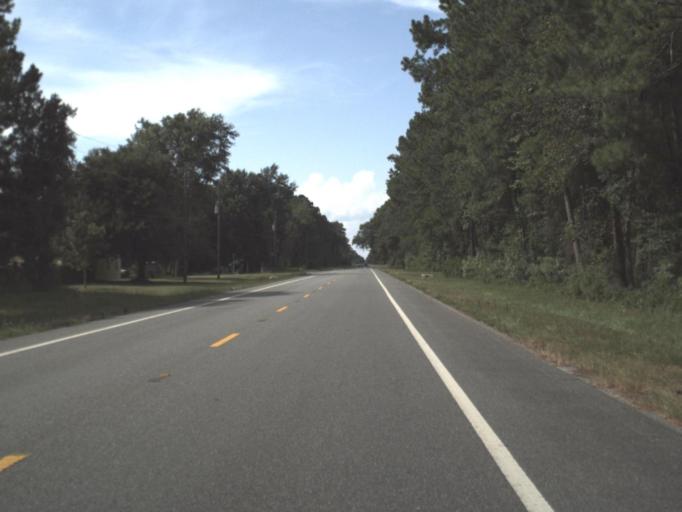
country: US
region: Florida
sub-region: Taylor County
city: Perry
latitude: 30.1753
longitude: -83.5986
